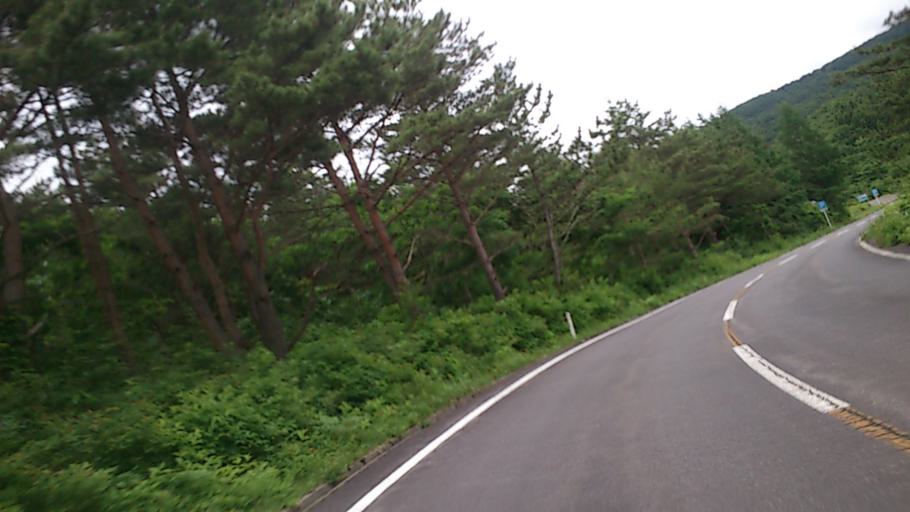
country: JP
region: Yamagata
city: Yuza
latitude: 39.1444
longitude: 139.9708
